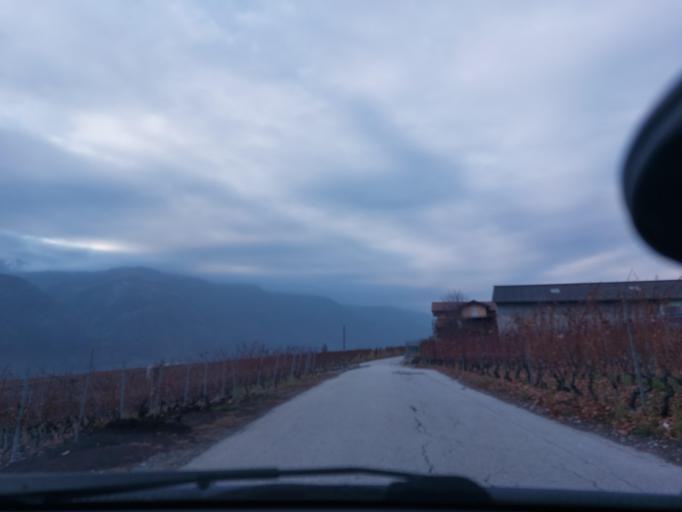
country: CH
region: Valais
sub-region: Conthey District
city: Chamoson
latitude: 46.2008
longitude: 7.2292
